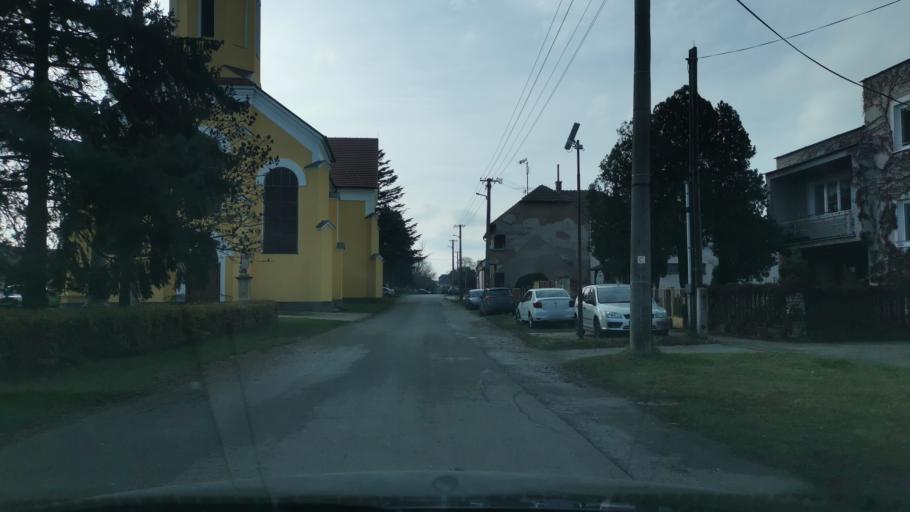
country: SK
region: Trnavsky
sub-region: Okres Skalica
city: Holic
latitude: 48.7888
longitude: 17.1140
